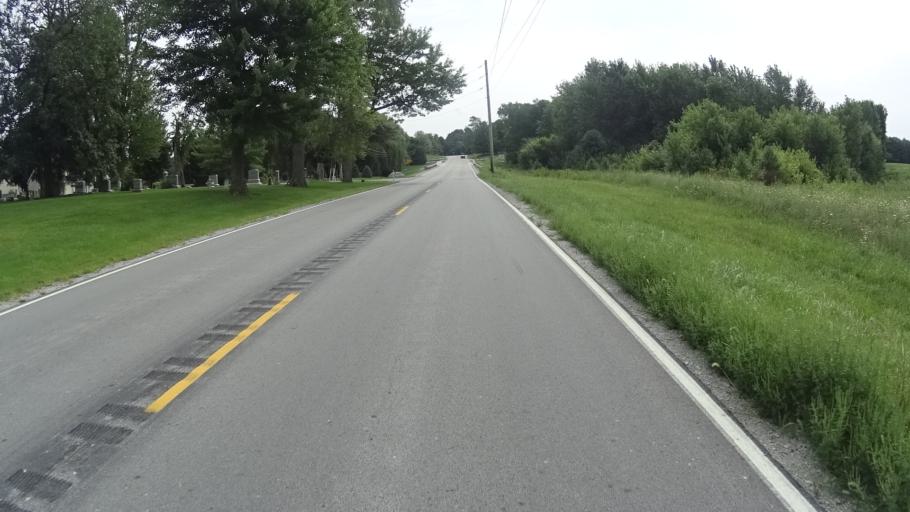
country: US
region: Indiana
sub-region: Madison County
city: Pendleton
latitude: 40.0096
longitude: -85.7921
